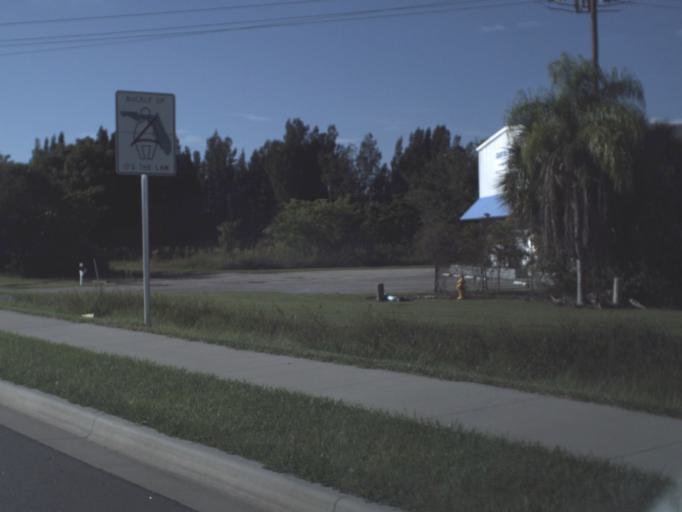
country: US
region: Florida
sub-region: Lee County
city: Palmona Park
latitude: 26.7048
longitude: -81.8955
